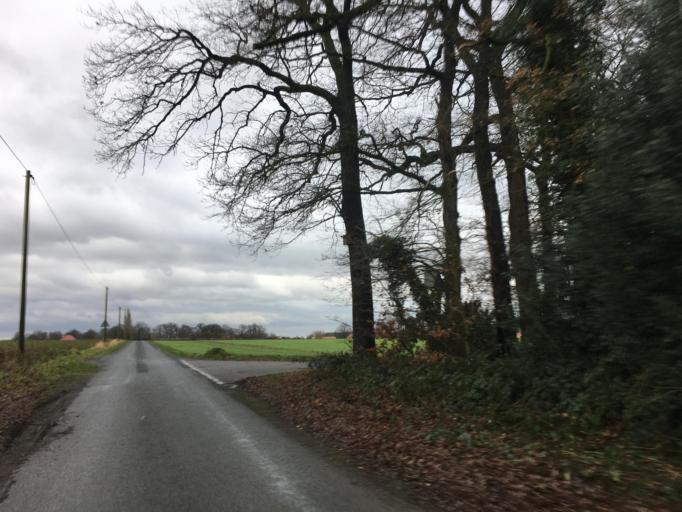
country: DE
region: North Rhine-Westphalia
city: Olfen
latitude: 51.7580
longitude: 7.3480
